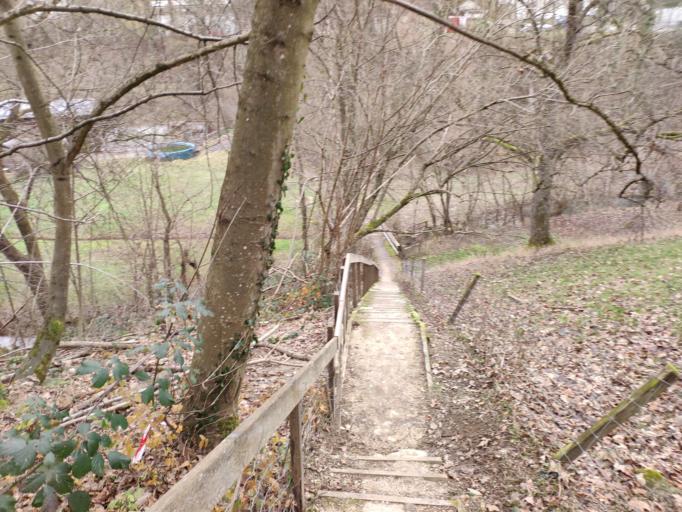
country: CH
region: Basel-City
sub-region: Basel-Stadt
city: Bettingen
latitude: 47.5847
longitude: 7.6725
